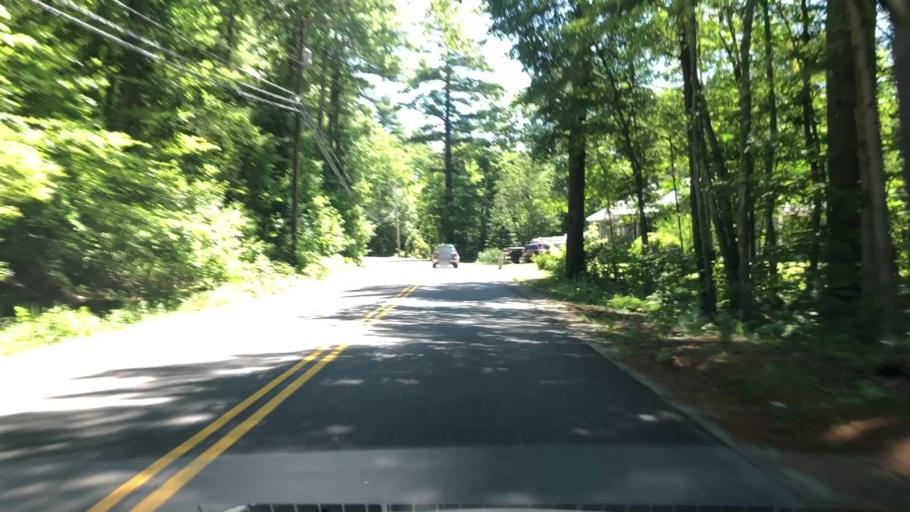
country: US
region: New Hampshire
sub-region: Hillsborough County
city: Milford
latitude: 42.8651
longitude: -71.6086
